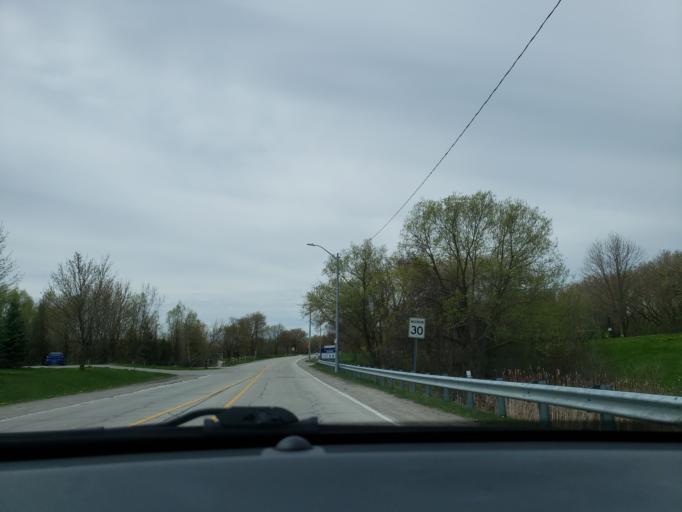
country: CA
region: Ontario
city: Newmarket
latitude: 44.0719
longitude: -79.4536
